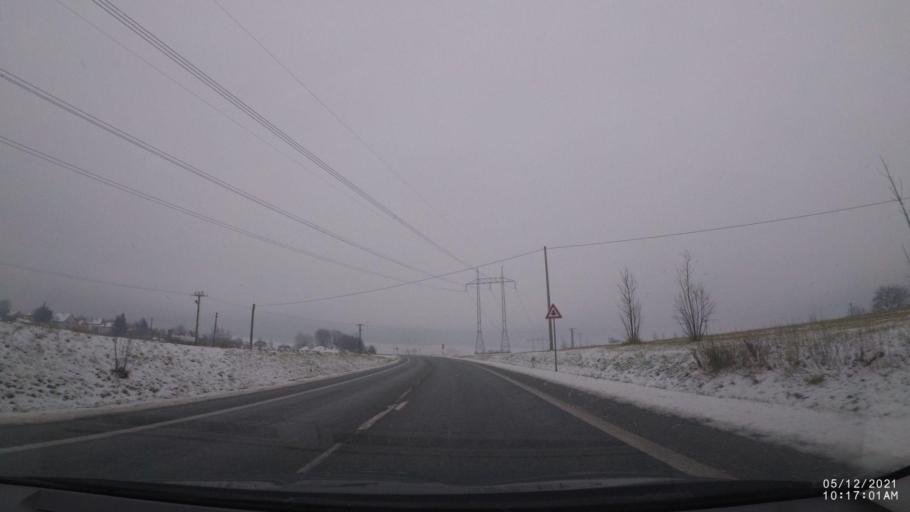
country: CZ
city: Vamberk
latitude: 50.1087
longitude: 16.2844
